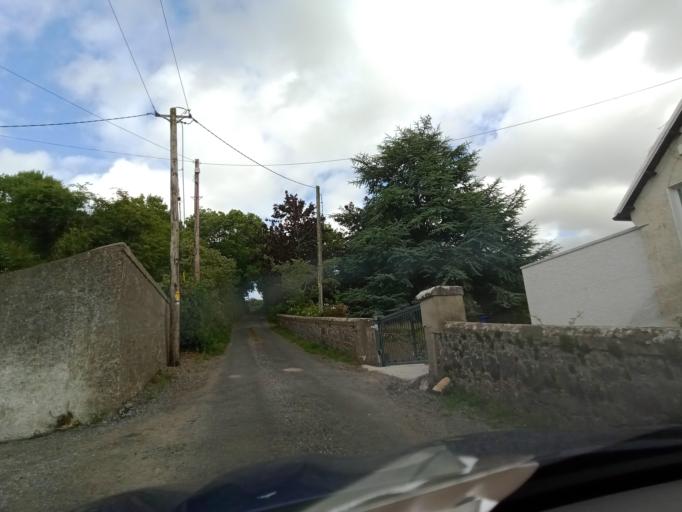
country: IE
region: Leinster
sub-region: Laois
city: Stradbally
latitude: 53.0304
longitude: -7.2096
